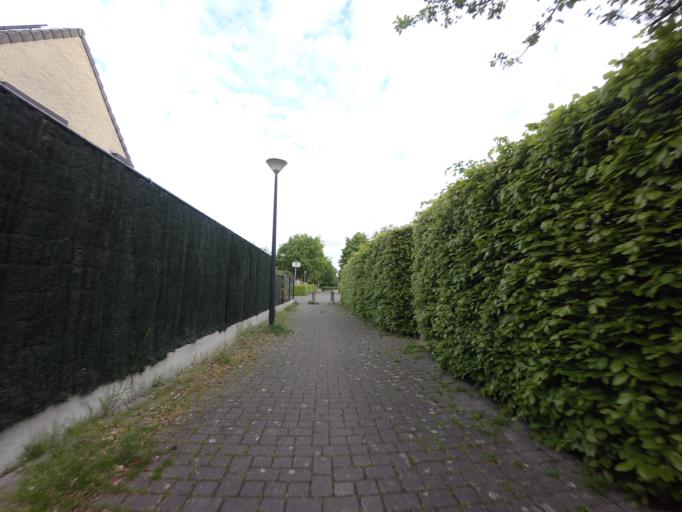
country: BE
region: Flanders
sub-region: Provincie Vlaams-Brabant
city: Vilvoorde
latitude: 50.9166
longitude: 4.3992
